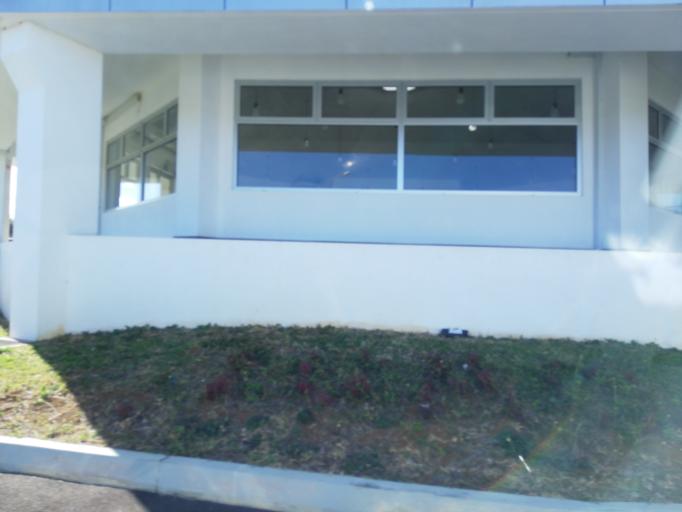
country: MU
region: Plaines Wilhems
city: Ebene
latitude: -20.2357
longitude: 57.5002
